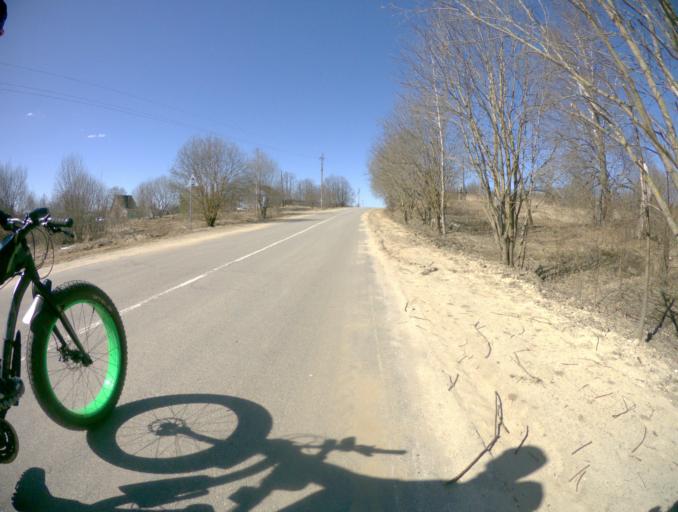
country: RU
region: Vladimir
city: Kameshkovo
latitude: 56.3473
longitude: 40.8025
